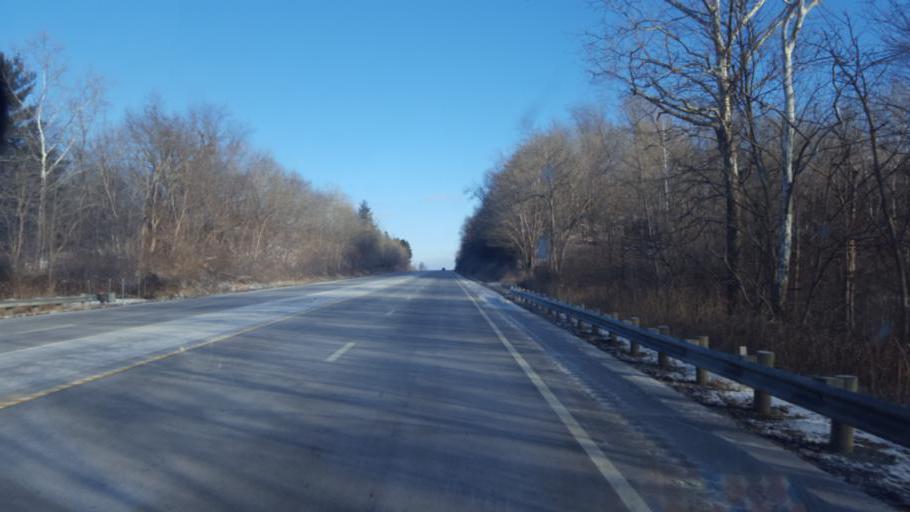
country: US
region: Ohio
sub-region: Pike County
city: Waverly
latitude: 39.1388
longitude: -82.9777
